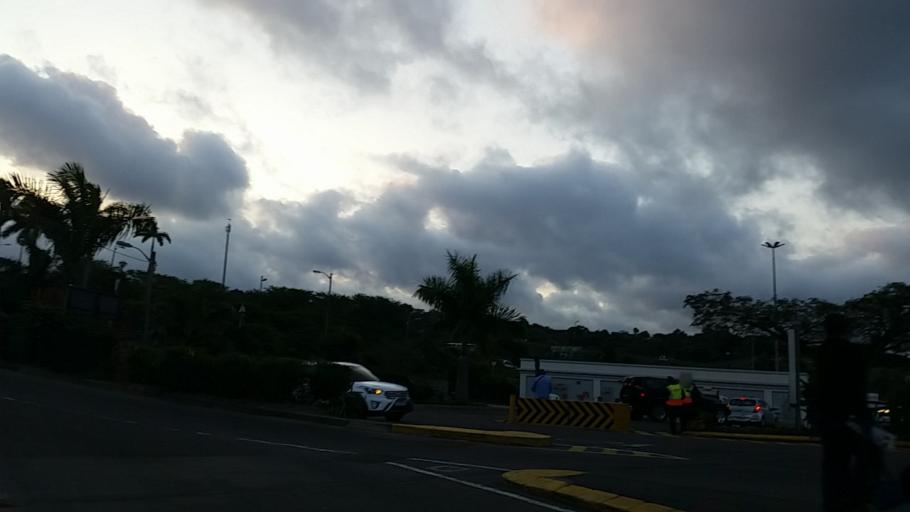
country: ZA
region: KwaZulu-Natal
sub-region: eThekwini Metropolitan Municipality
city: Berea
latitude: -29.8501
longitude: 30.9337
